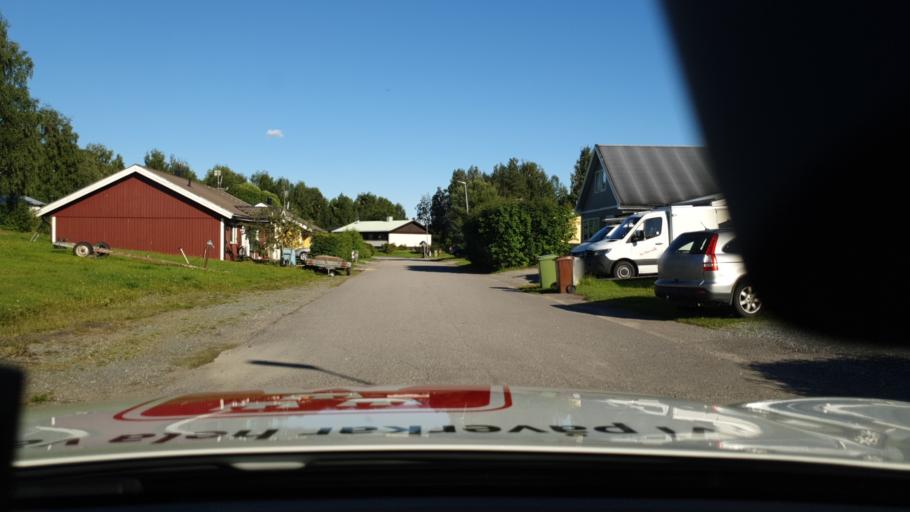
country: SE
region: Norrbotten
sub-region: Alvsbyns Kommun
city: AElvsbyn
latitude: 65.6668
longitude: 20.8646
